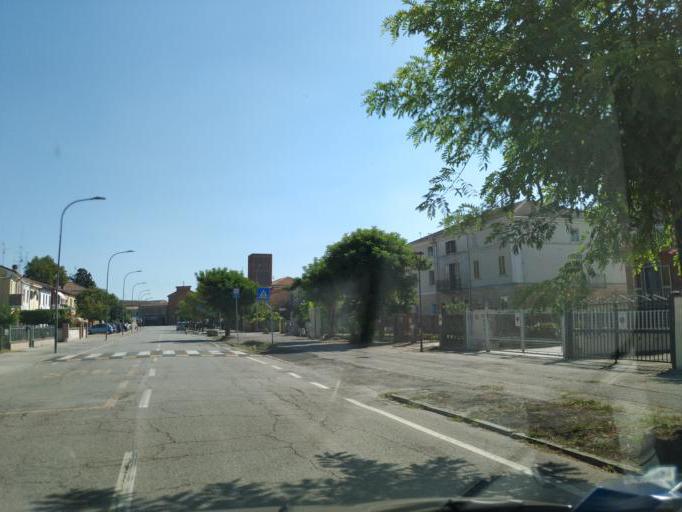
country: IT
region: Emilia-Romagna
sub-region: Provincia di Ferrara
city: Coccanile-Cesta
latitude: 44.9124
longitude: 11.9091
